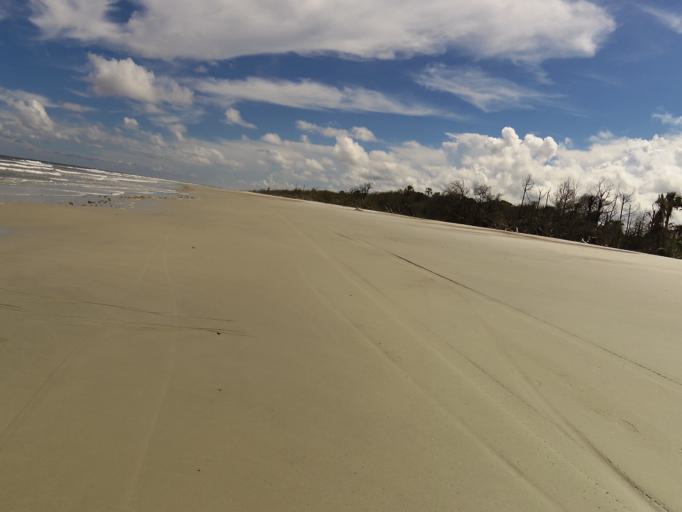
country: US
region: Florida
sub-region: Duval County
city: Atlantic Beach
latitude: 30.4749
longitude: -81.4130
